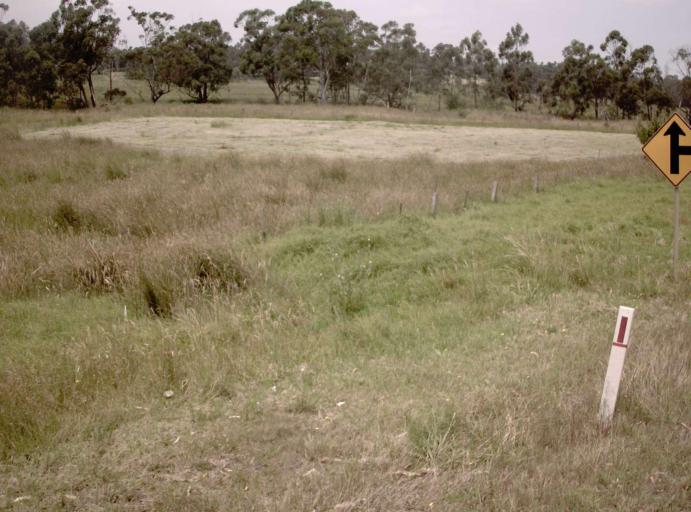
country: AU
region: Victoria
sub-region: Latrobe
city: Traralgon
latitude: -38.4648
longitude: 146.7189
